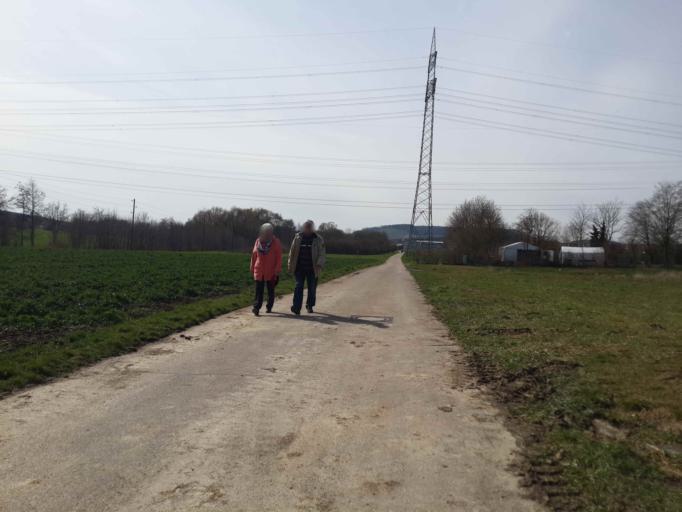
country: DE
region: Baden-Wuerttemberg
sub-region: Regierungsbezirk Stuttgart
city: Nordheim
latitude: 49.1022
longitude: 9.1213
